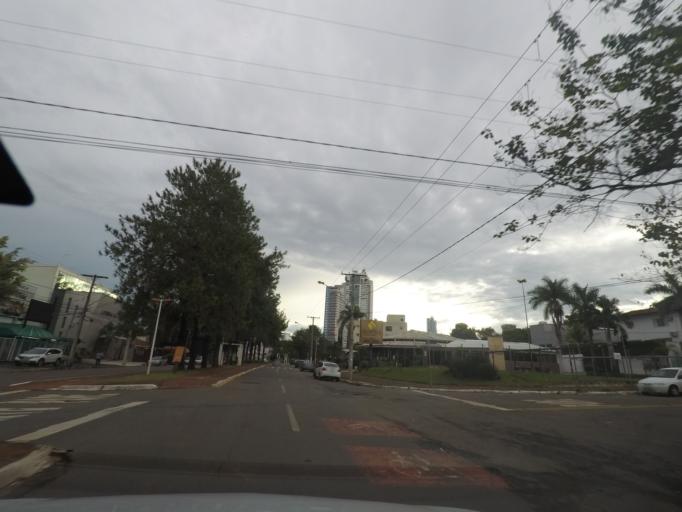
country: BR
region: Goias
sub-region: Goiania
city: Goiania
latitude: -16.7031
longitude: -49.2586
